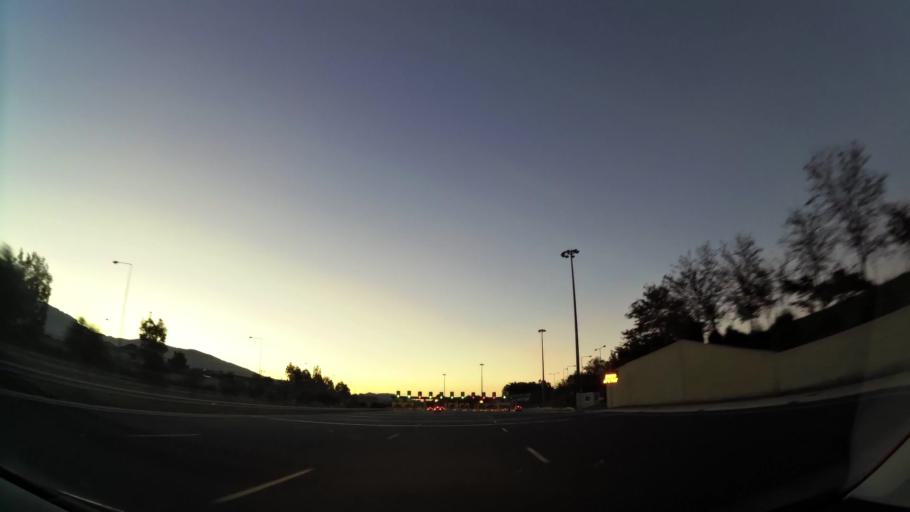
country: GR
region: Attica
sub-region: Nomarchia Anatolikis Attikis
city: Pallini
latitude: 37.9933
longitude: 23.8892
